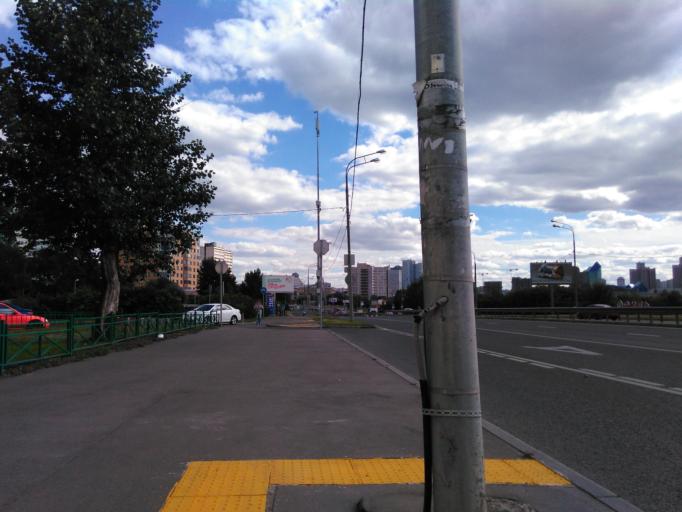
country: RU
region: Moscow
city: Nikol'skoye
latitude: 55.6793
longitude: 37.4828
